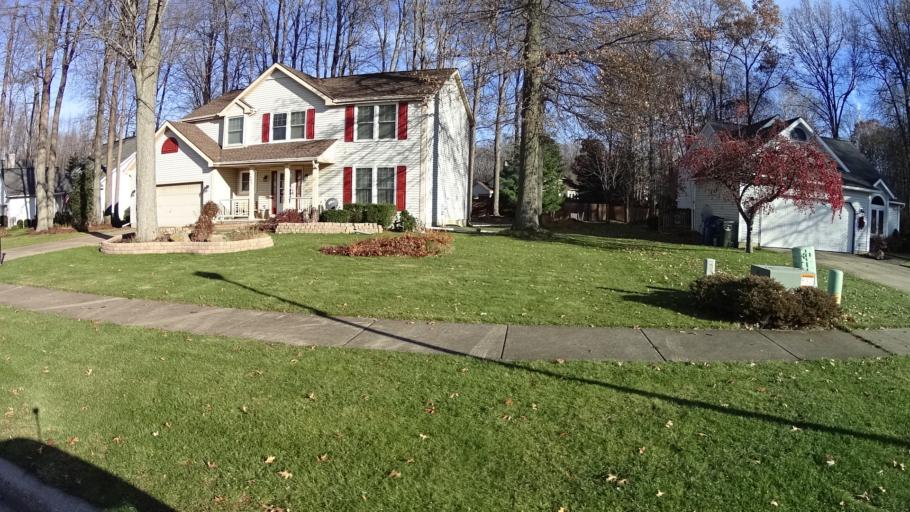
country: US
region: Ohio
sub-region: Lorain County
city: North Ridgeville
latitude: 41.3892
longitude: -81.9880
